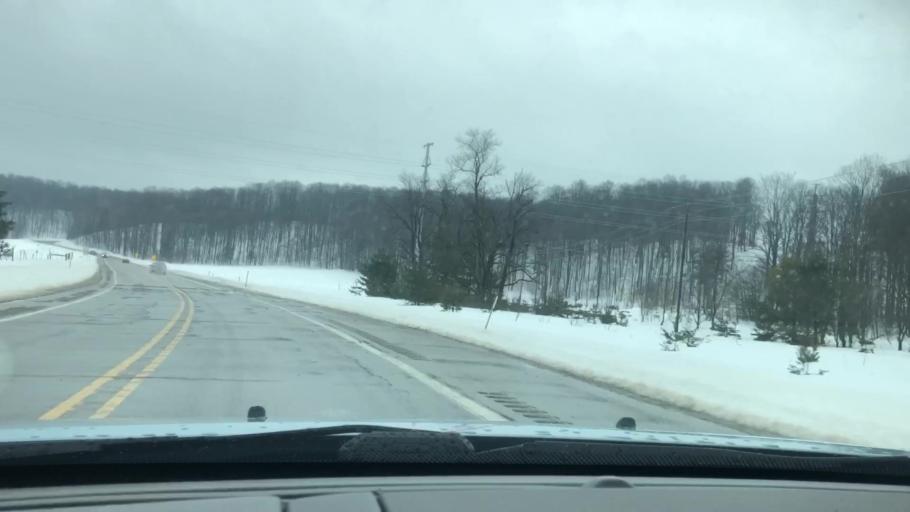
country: US
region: Michigan
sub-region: Charlevoix County
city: Boyne City
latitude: 45.0812
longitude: -84.9200
